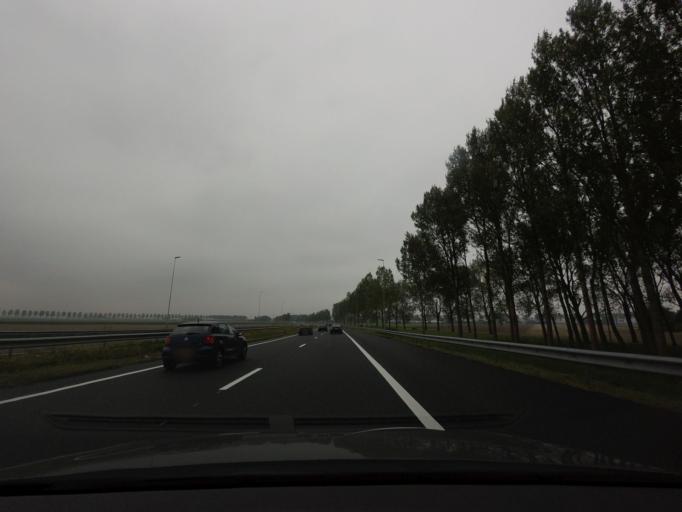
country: NL
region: South Holland
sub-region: Gemeente Kaag en Braassem
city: Oude Wetering
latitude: 52.2305
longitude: 4.6109
